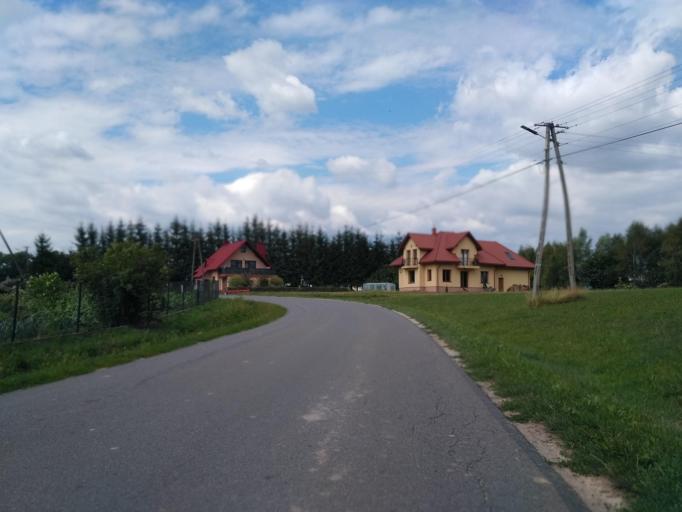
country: PL
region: Subcarpathian Voivodeship
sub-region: Powiat rzeszowski
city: Chmielnik
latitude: 49.9508
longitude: 22.1482
